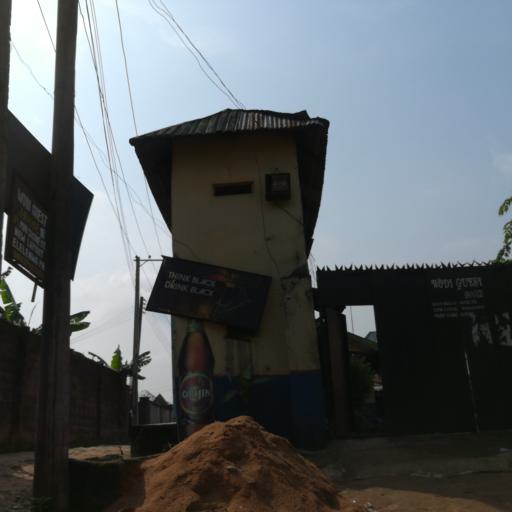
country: NG
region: Rivers
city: Port Harcourt
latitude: 4.8410
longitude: 7.0631
